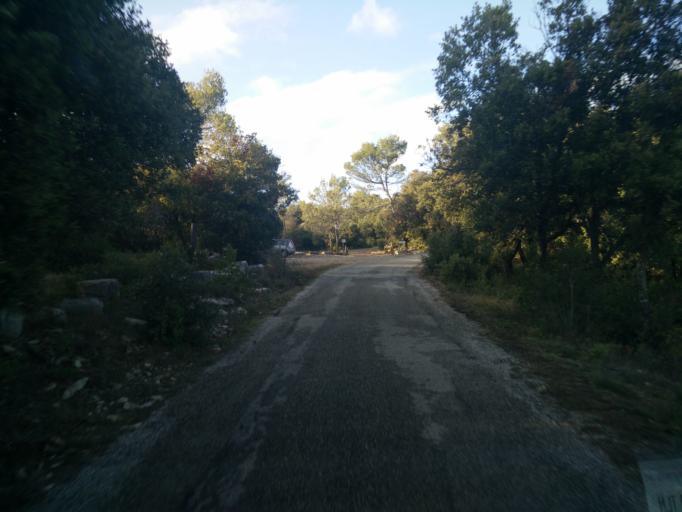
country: FR
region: Provence-Alpes-Cote d'Azur
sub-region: Departement du Var
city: Le Revest-les-Eaux
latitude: 43.2319
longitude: 5.9098
